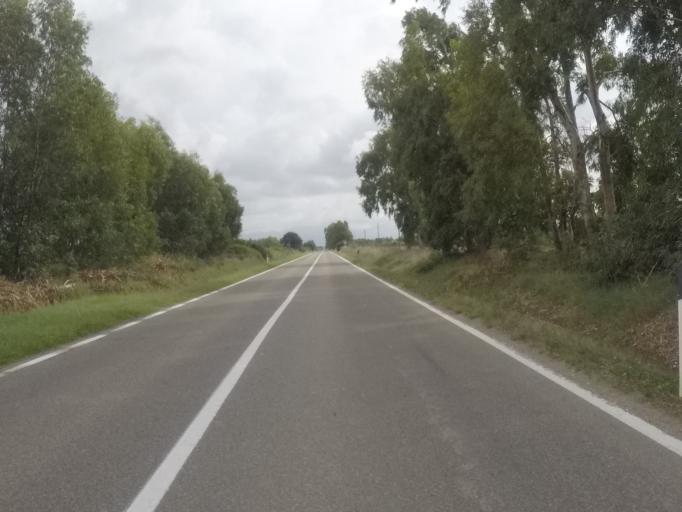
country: IT
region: Sardinia
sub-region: Provincia di Oristano
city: San Nicolo d'Arcidano
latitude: 39.6554
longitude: 8.6535
